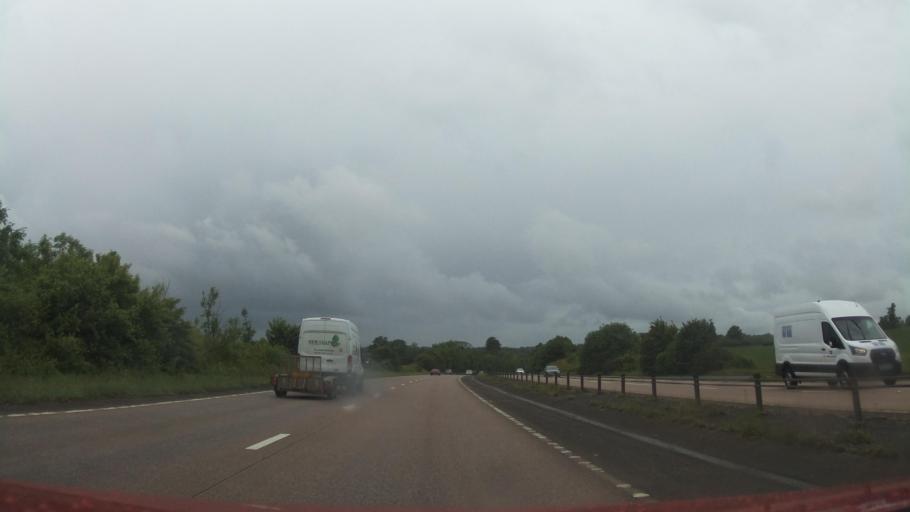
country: GB
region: England
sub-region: Devon
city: Ottery St Mary
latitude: 50.7710
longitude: -3.2858
